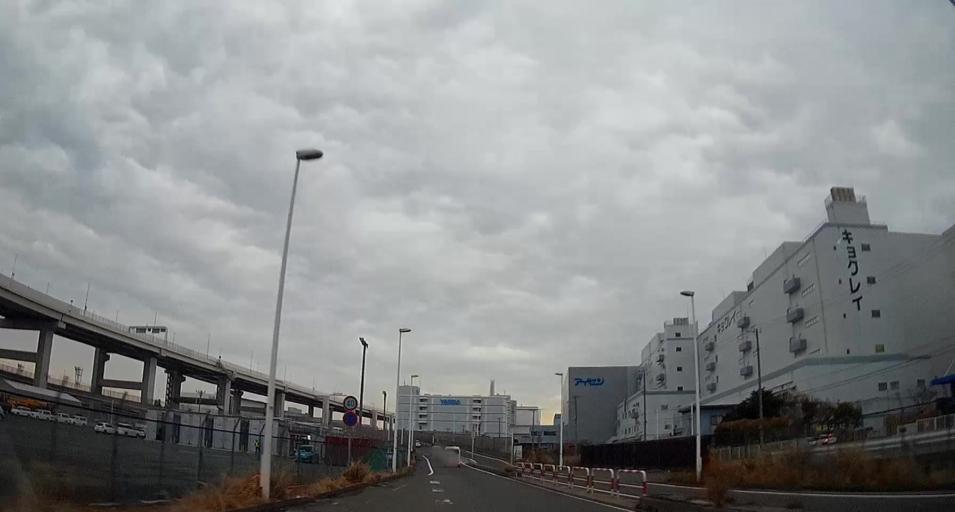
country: JP
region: Kanagawa
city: Yokohama
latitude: 35.4636
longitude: 139.6842
